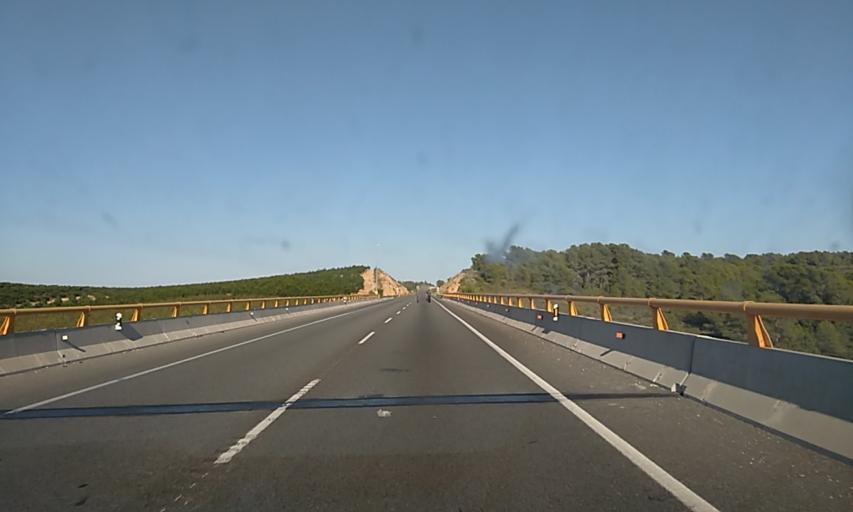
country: ES
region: Valencia
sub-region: Provincia de Castello
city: Torreblanca
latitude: 40.2135
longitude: 0.1490
